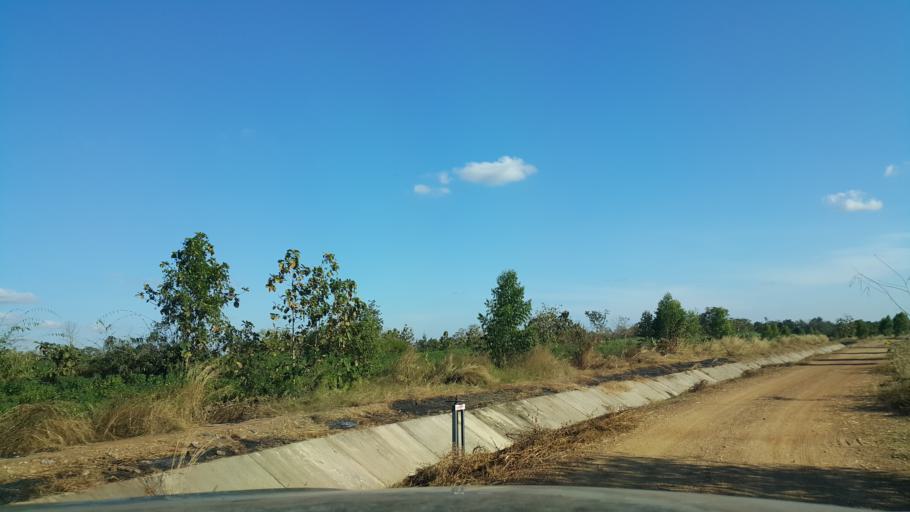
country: TH
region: Sukhothai
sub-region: Amphoe Si Satchanalai
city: Si Satchanalai
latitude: 17.4737
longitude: 99.6586
